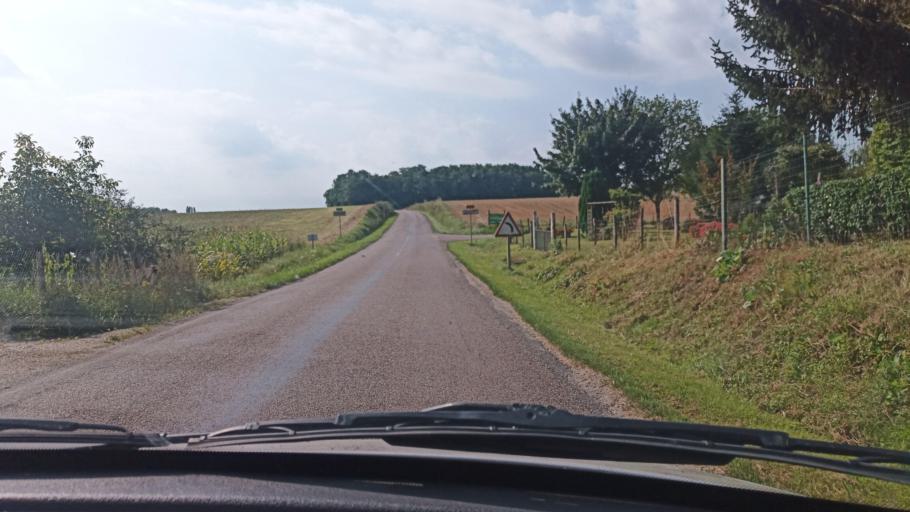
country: FR
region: Bourgogne
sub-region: Departement de l'Yonne
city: Saint-Valerien
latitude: 48.2101
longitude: 3.0735
